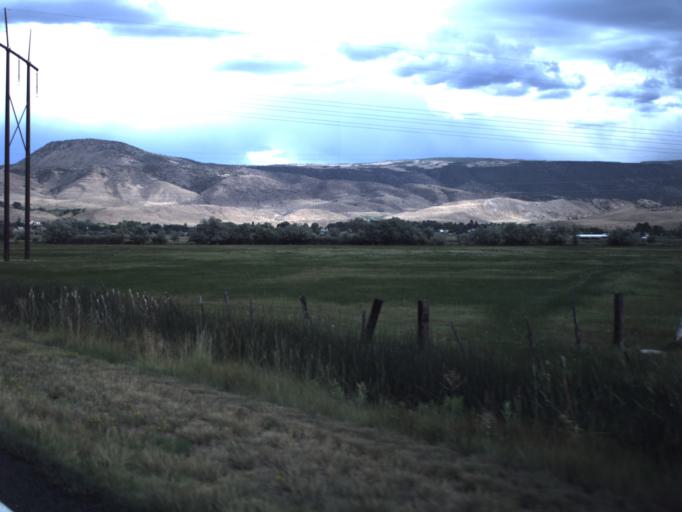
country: US
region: Utah
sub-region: Sevier County
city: Richfield
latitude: 38.7742
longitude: -112.0096
